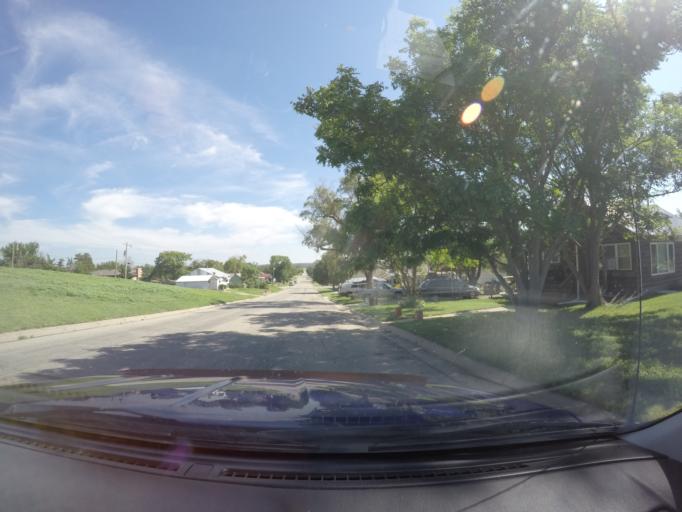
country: US
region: Kansas
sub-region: Rooks County
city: Stockton
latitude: 39.4399
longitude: -99.2709
